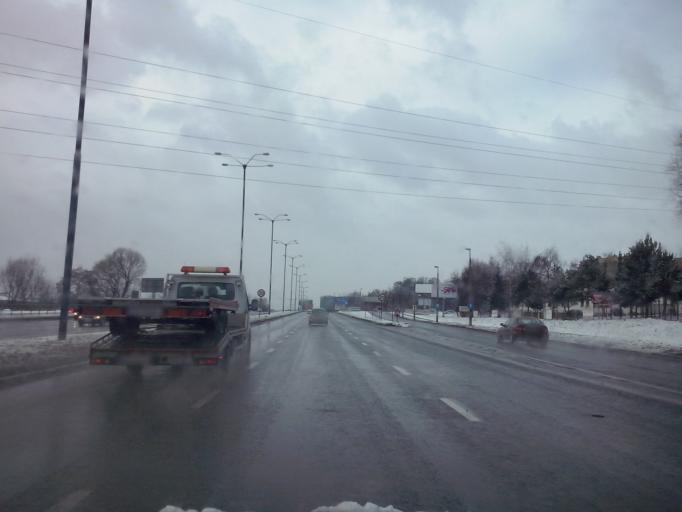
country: PL
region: Lesser Poland Voivodeship
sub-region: Krakow
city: Krakow
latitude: 50.0876
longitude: 19.9985
